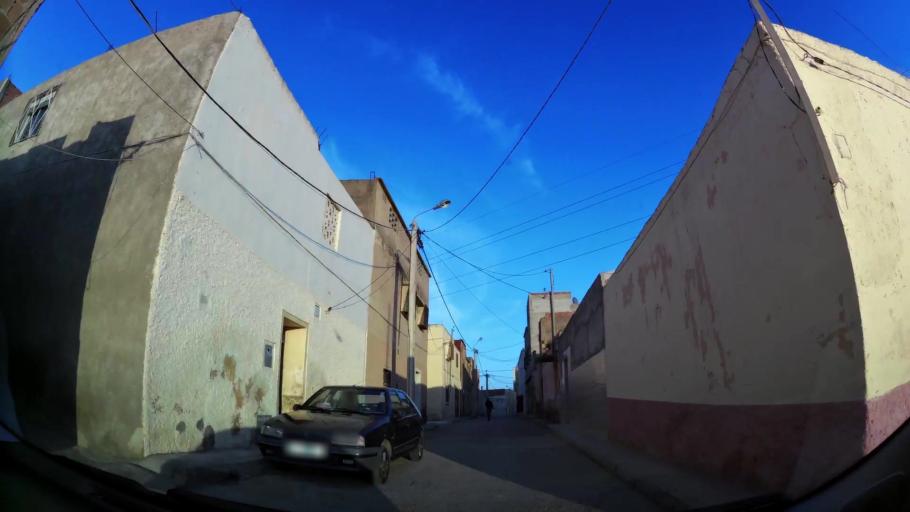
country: MA
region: Oriental
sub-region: Oujda-Angad
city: Oujda
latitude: 34.7036
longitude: -1.9242
